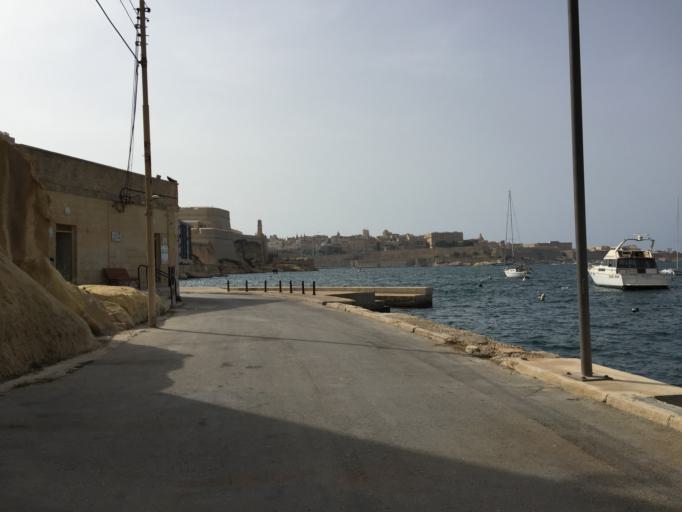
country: MT
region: Il-Birgu
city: Vittoriosa
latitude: 35.8896
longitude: 14.5221
